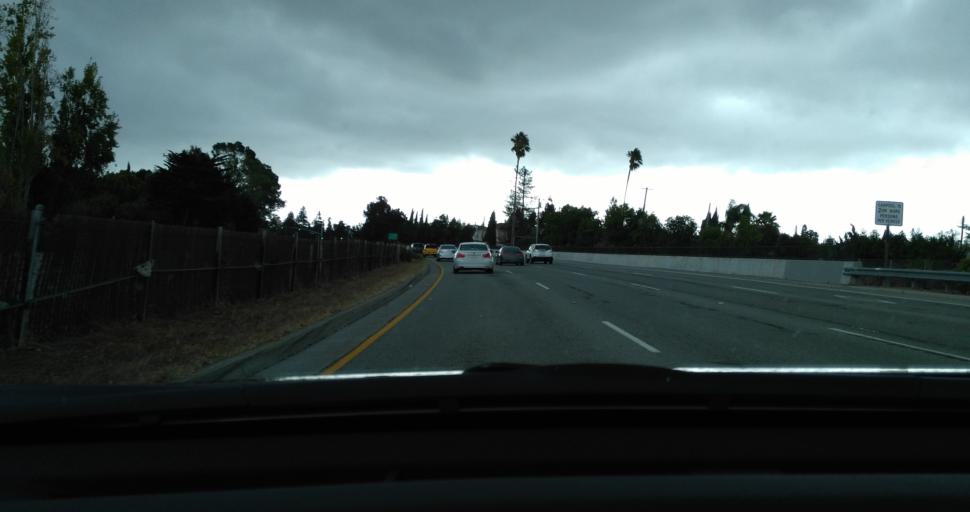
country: US
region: California
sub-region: Santa Clara County
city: Santa Clara
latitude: 37.3619
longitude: -121.9681
